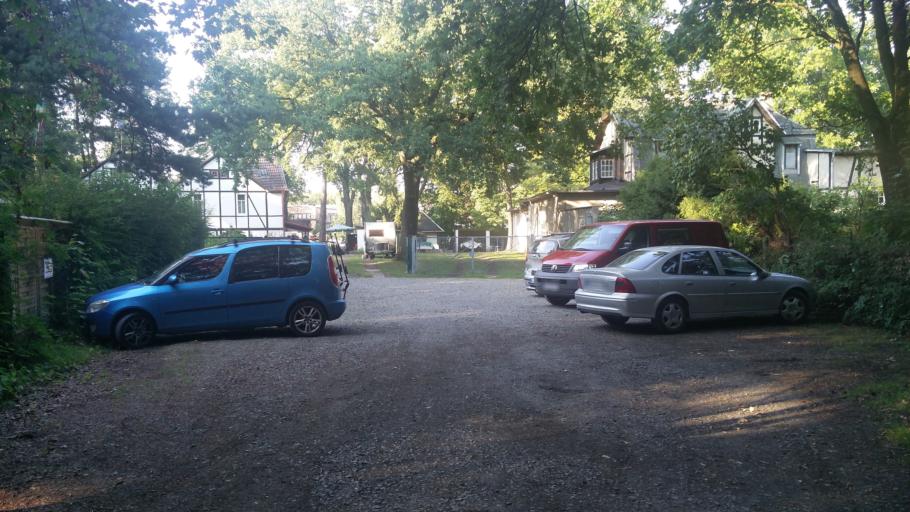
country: DE
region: Berlin
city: Friedrichshagen
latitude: 52.4465
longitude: 13.6064
